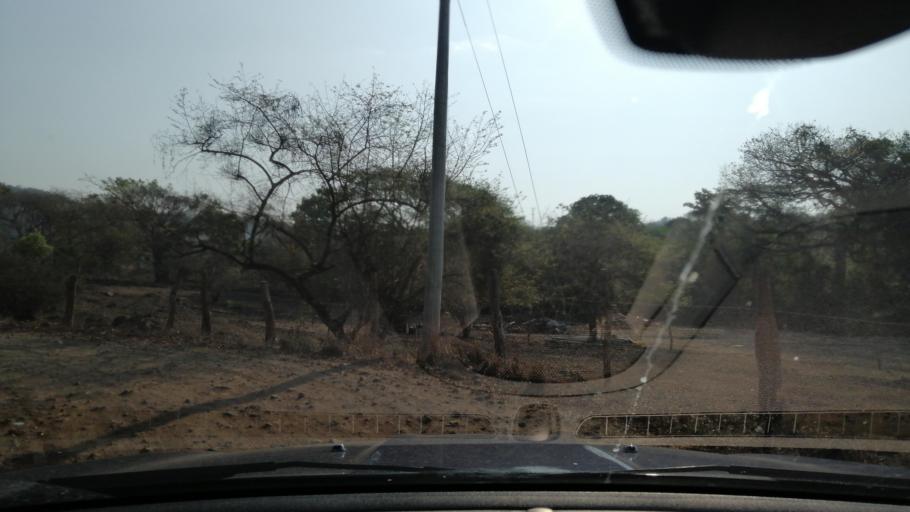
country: SV
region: Santa Ana
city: Texistepeque
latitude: 14.2182
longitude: -89.4594
